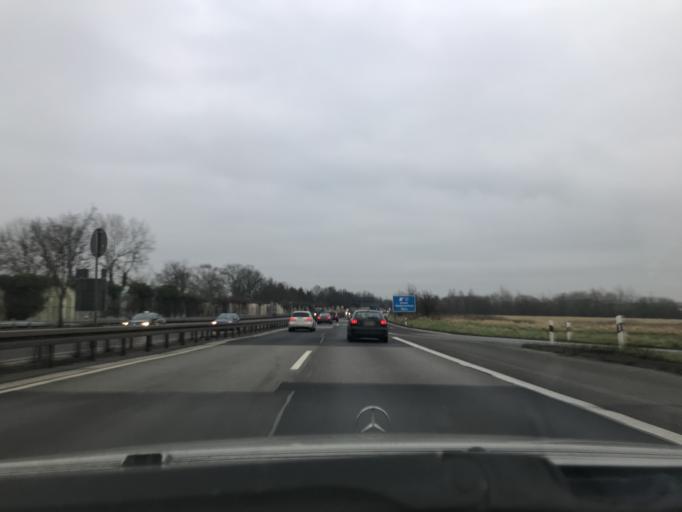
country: DE
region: Hesse
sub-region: Regierungsbezirk Kassel
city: Fuldabruck
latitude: 51.2650
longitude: 9.4518
